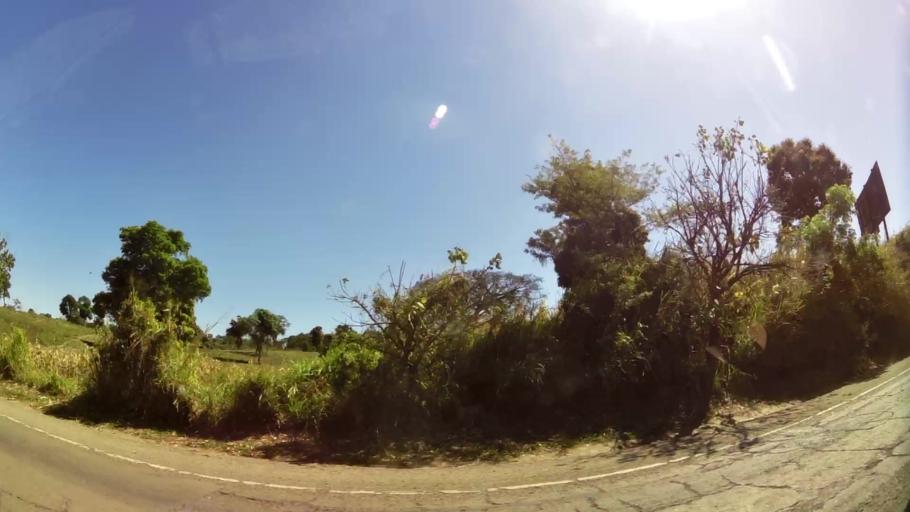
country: SV
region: Ahuachapan
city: Ahuachapan
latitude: 13.9429
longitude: -89.8418
